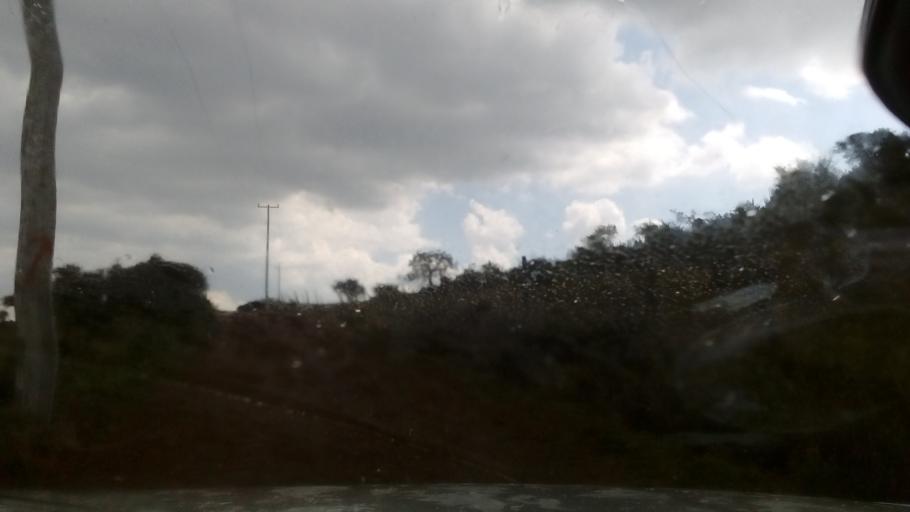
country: MX
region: Guanajuato
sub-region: Silao de la Victoria
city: San Francisco (Banos de Agua Caliente)
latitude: 21.1559
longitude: -101.4380
